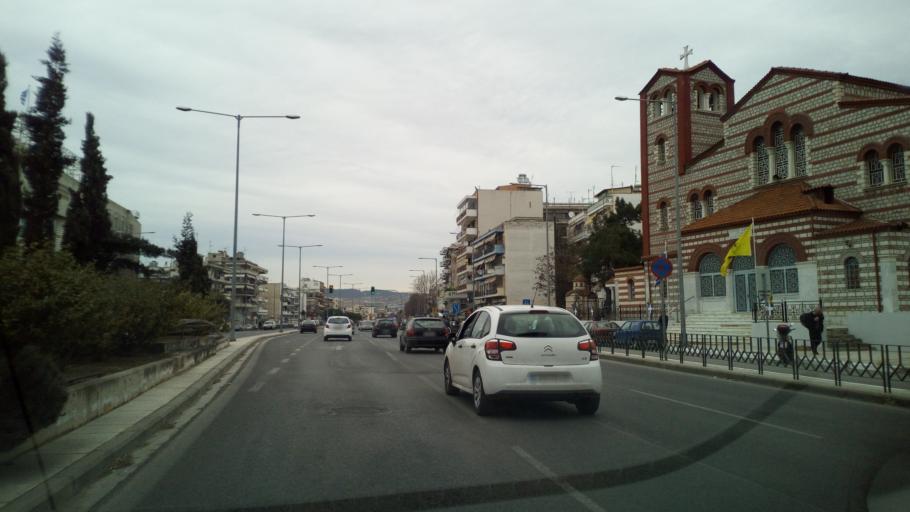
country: GR
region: Central Macedonia
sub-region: Nomos Thessalonikis
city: Stavroupoli
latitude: 40.6637
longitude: 22.9362
